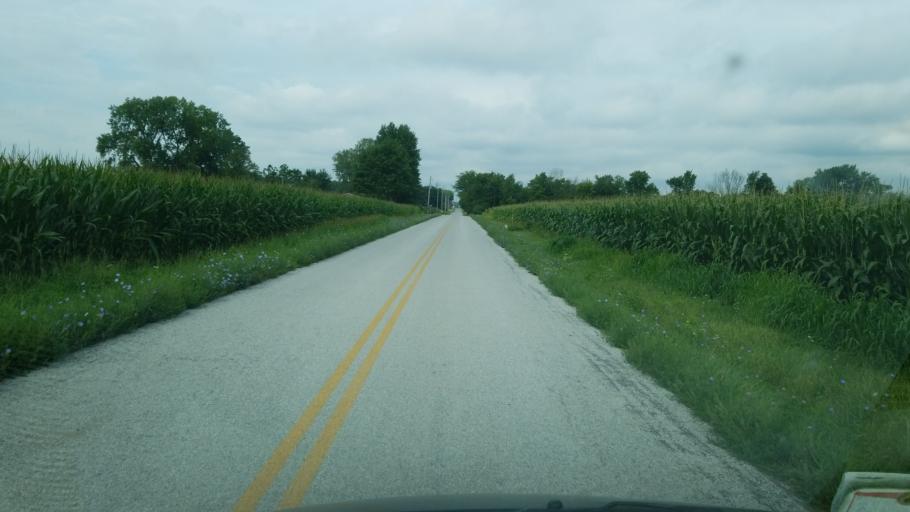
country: US
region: Ohio
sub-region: Sandusky County
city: Green Springs
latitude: 41.1894
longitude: -83.1124
